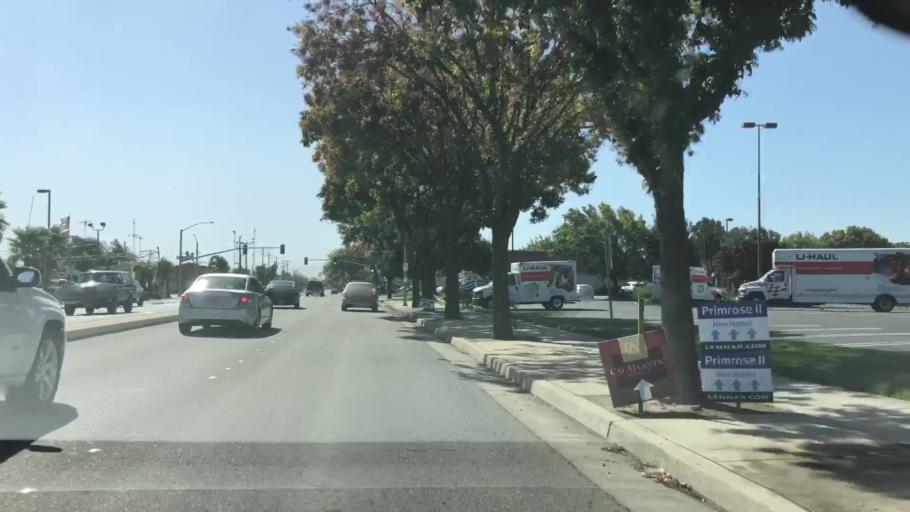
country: US
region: California
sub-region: San Joaquin County
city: Tracy
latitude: 37.7554
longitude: -121.4352
